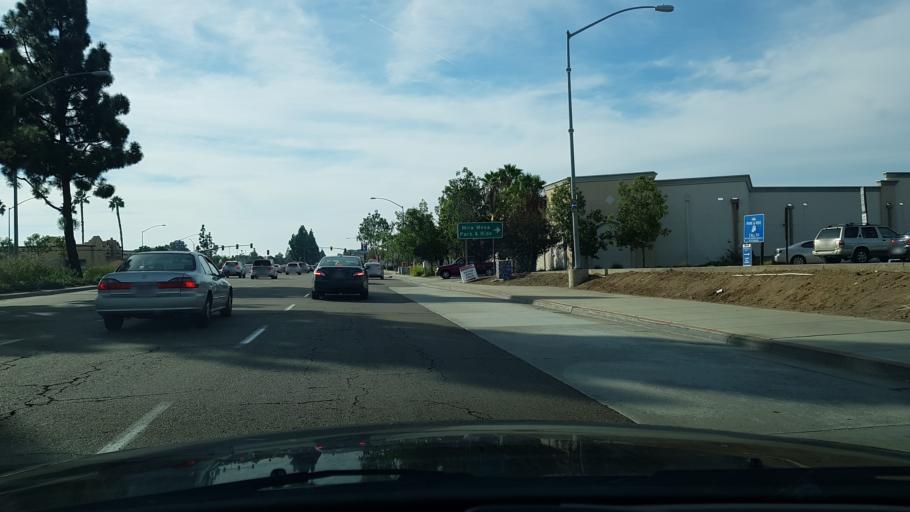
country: US
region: California
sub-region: San Diego County
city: Poway
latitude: 32.9174
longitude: -117.1183
